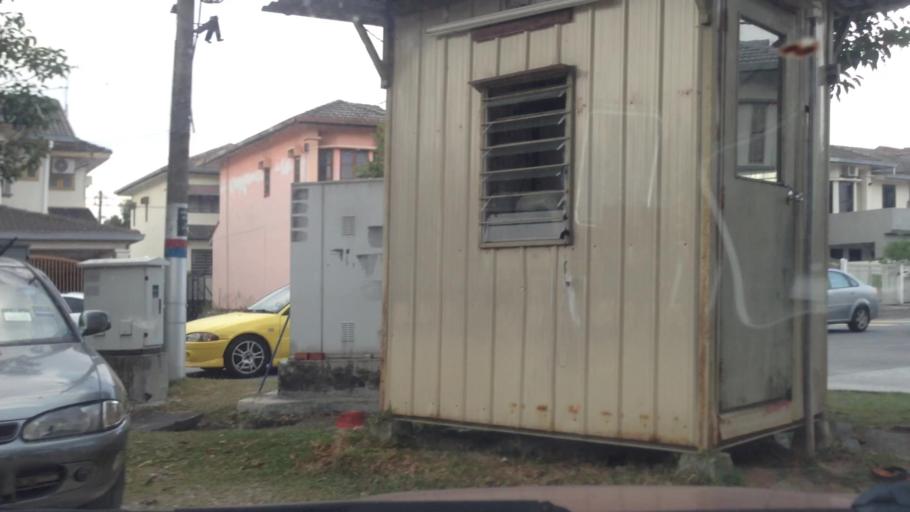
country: MY
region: Selangor
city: Subang Jaya
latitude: 3.0392
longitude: 101.5762
